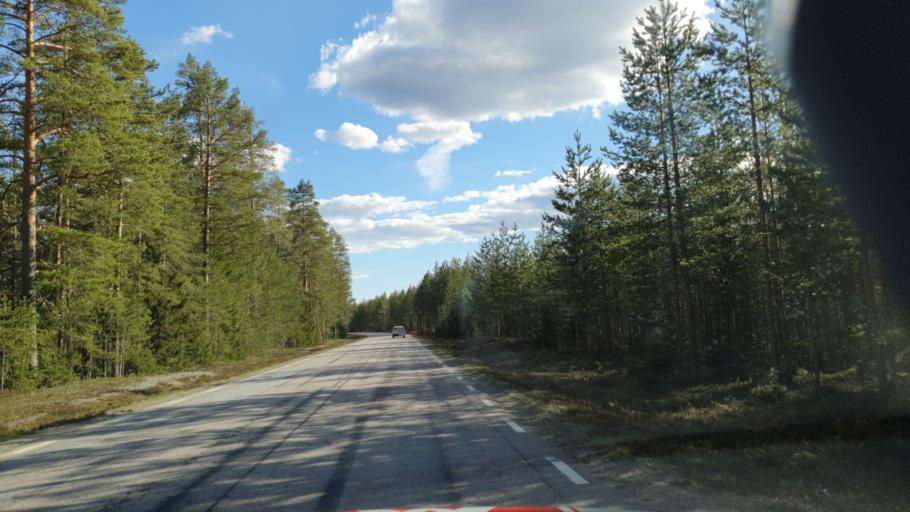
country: SE
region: Vaesterbotten
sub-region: Umea Kommun
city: Roback
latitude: 63.8692
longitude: 20.1473
